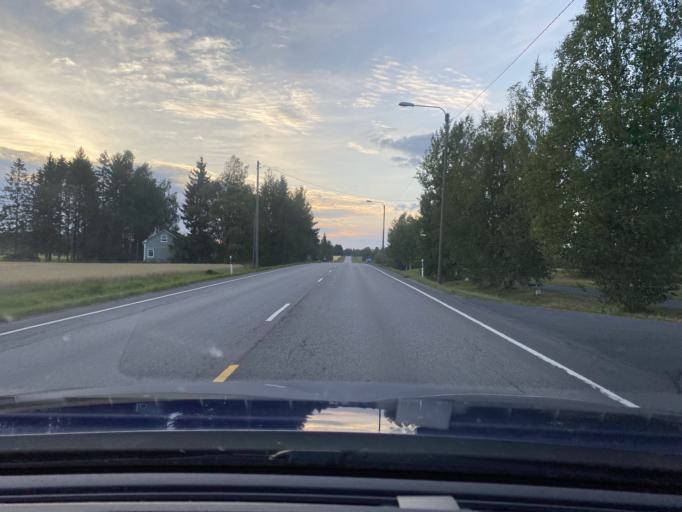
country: FI
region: Satakunta
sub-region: Pohjois-Satakunta
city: Kankaanpaeae
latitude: 61.7471
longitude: 22.5204
